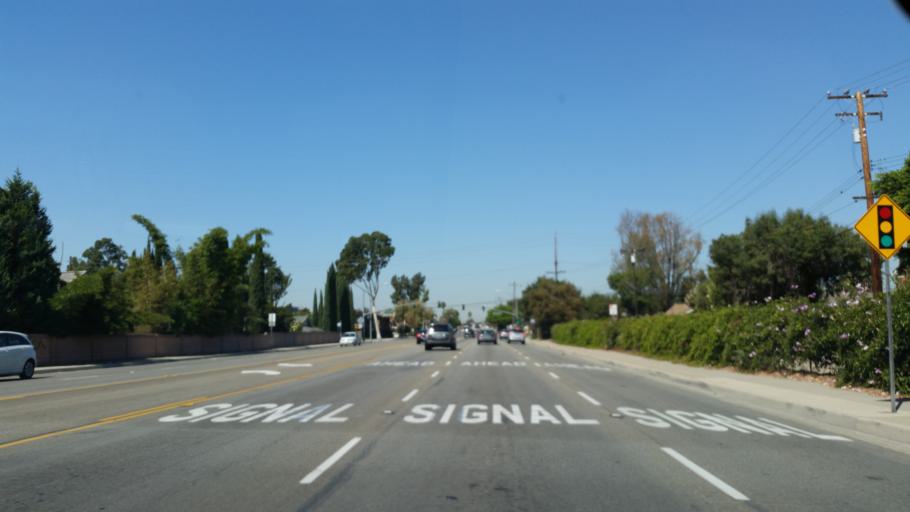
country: US
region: California
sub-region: Orange County
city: North Tustin
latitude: 33.7438
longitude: -117.8029
